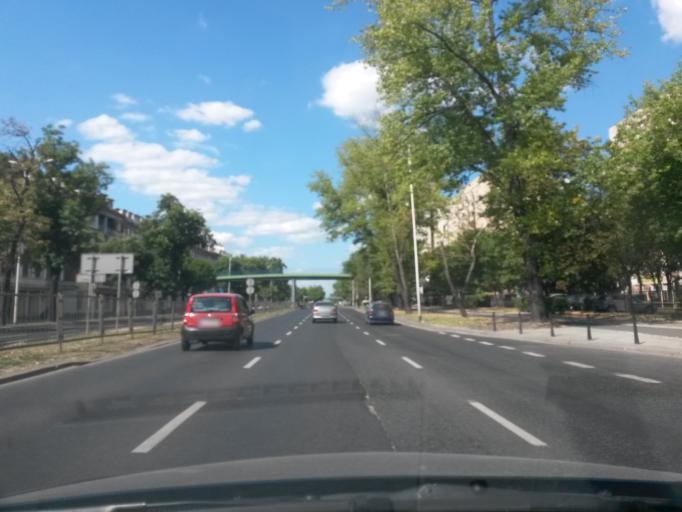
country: PL
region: Masovian Voivodeship
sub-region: Warszawa
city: Mokotow
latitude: 52.2082
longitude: 21.0484
